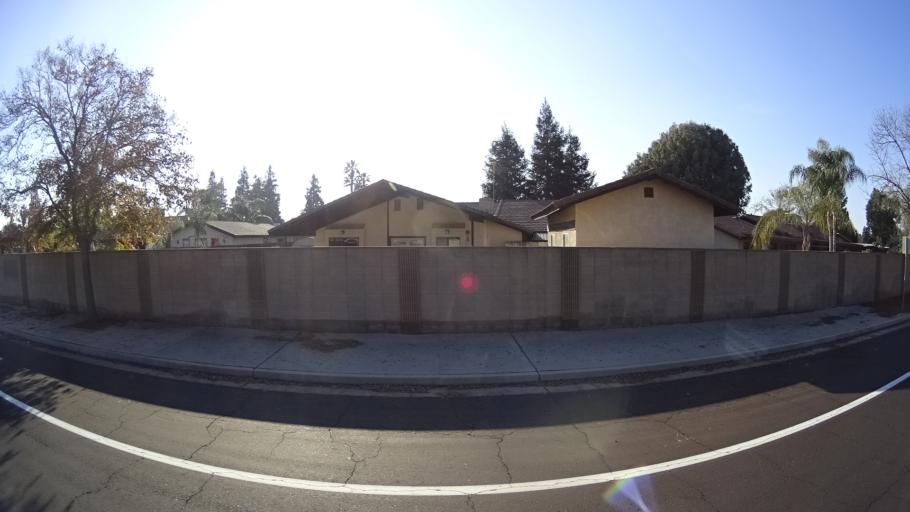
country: US
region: California
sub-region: Kern County
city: Greenacres
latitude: 35.3320
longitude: -119.0860
